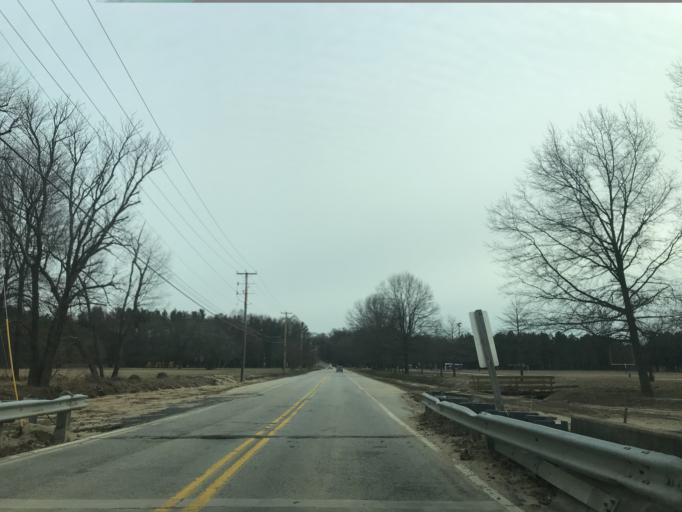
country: US
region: Maryland
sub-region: Cecil County
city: Elkton
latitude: 39.6087
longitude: -75.8217
